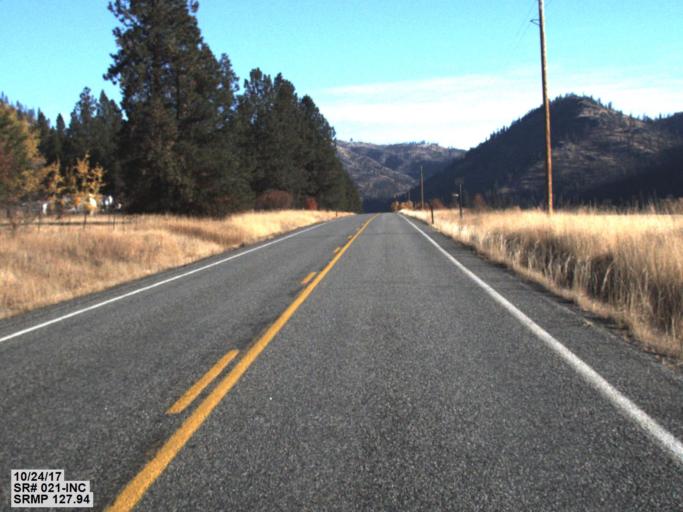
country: US
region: Washington
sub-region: Okanogan County
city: Coulee Dam
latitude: 48.2321
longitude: -118.7005
